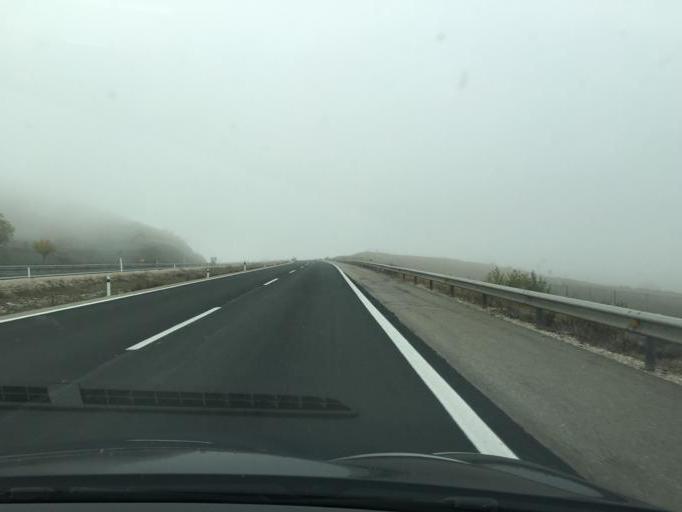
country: ES
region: Castille and Leon
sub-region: Provincia de Burgos
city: Villanueva de Teba
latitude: 42.6243
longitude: -3.1473
